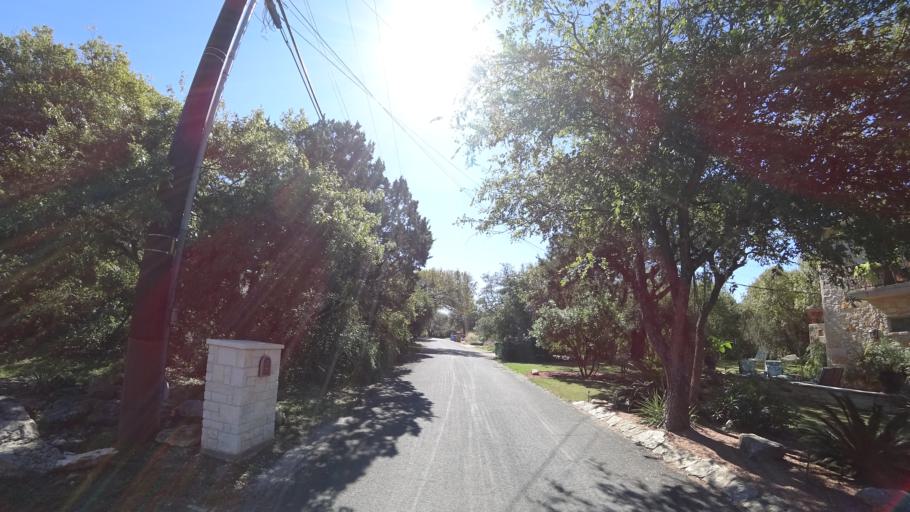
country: US
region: Texas
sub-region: Travis County
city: West Lake Hills
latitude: 30.3178
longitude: -97.8055
